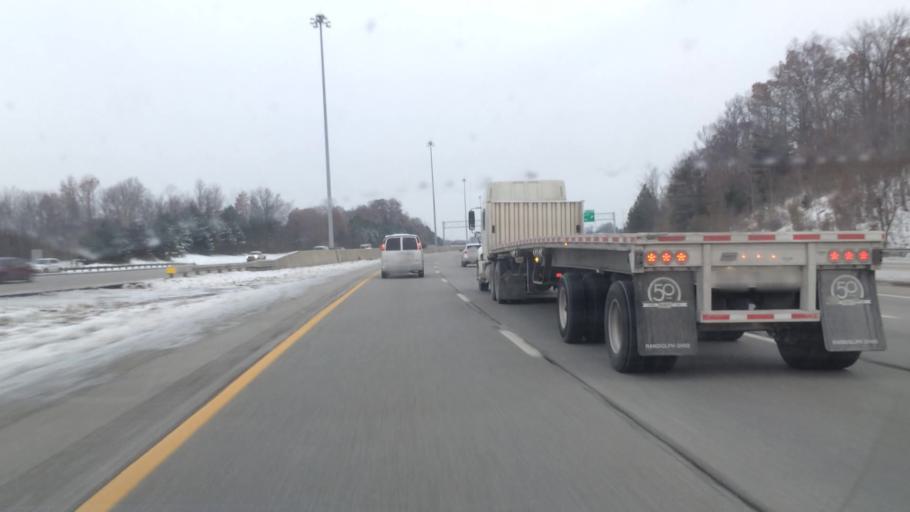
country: US
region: Ohio
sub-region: Cuyahoga County
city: Seven Hills
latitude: 41.4129
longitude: -81.6718
